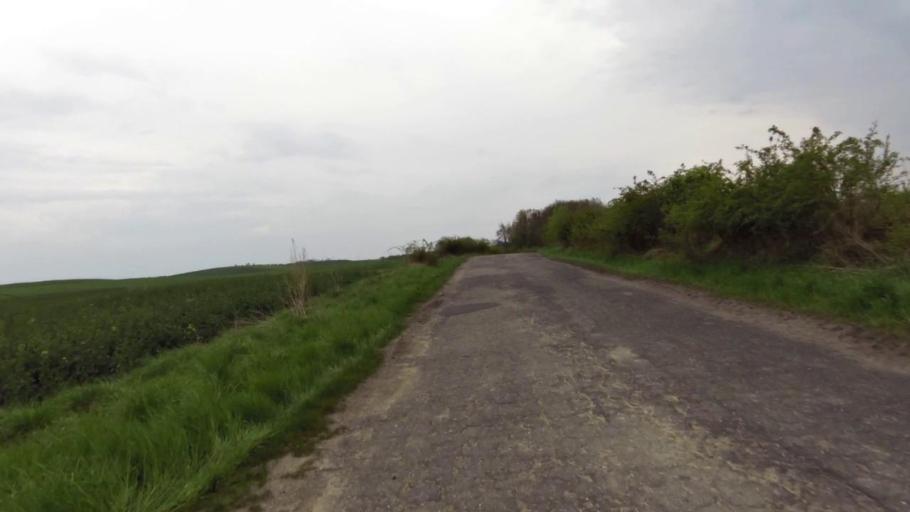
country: PL
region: West Pomeranian Voivodeship
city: Trzcinsko Zdroj
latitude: 52.9524
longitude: 14.6928
